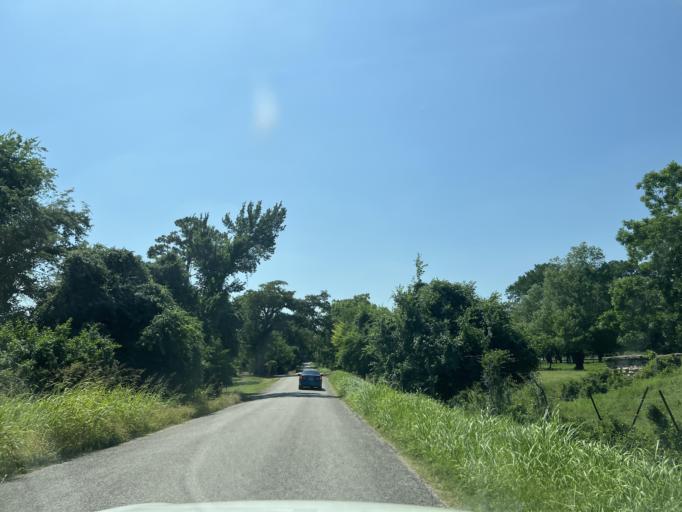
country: US
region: Texas
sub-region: Washington County
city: Brenham
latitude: 30.1577
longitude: -96.5160
